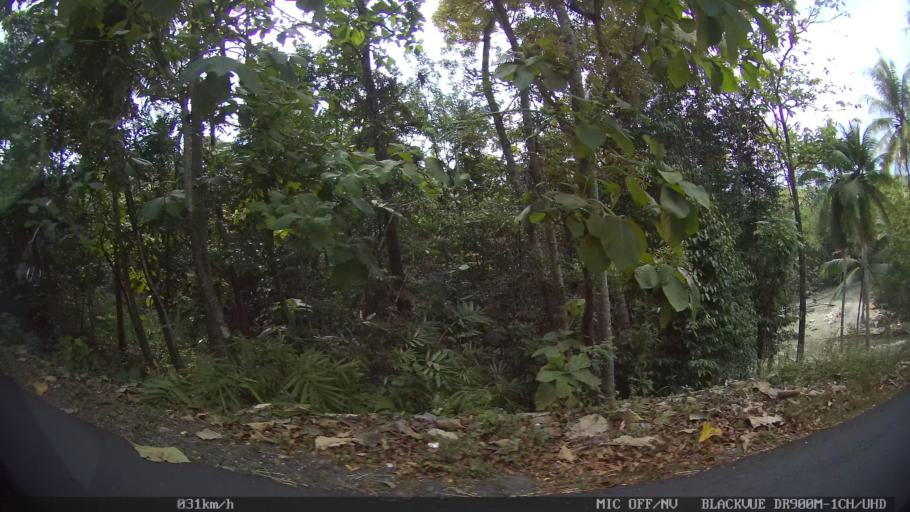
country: ID
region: Daerah Istimewa Yogyakarta
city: Kasihan
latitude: -7.8534
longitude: 110.3132
